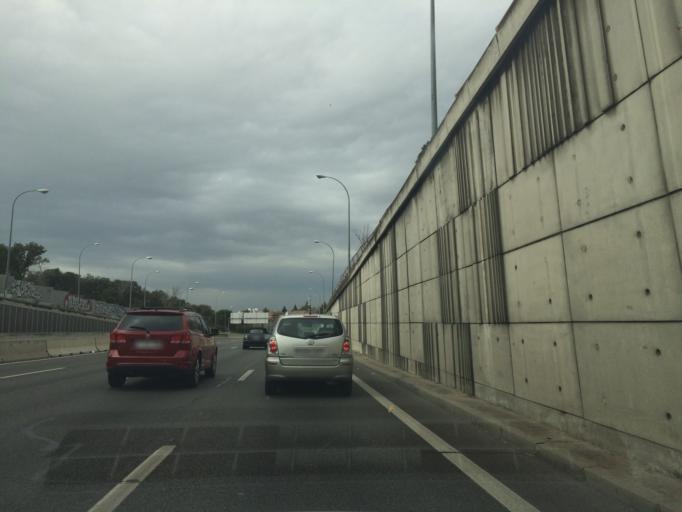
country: ES
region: Madrid
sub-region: Provincia de Madrid
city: Tetuan de las Victorias
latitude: 40.4732
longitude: -3.7364
